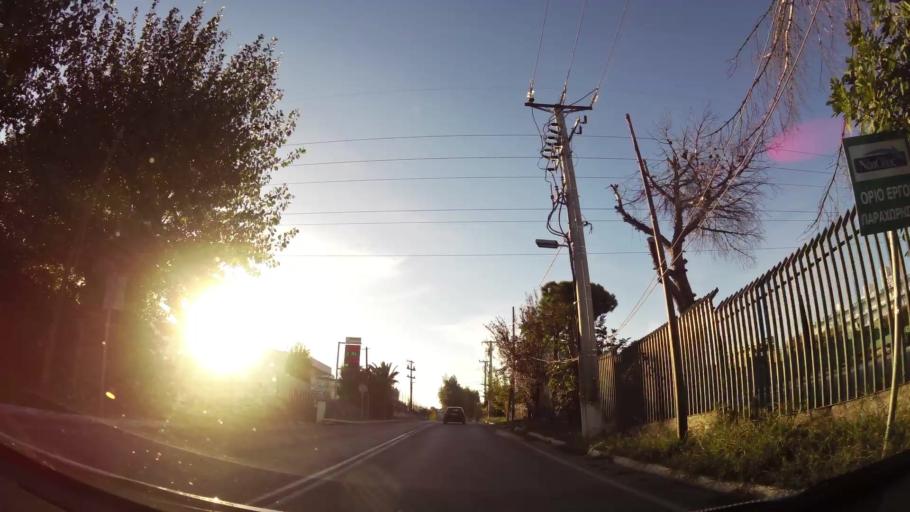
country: GR
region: Attica
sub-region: Nomarchia Anatolikis Attikis
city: Kryoneri
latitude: 38.1407
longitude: 23.8385
